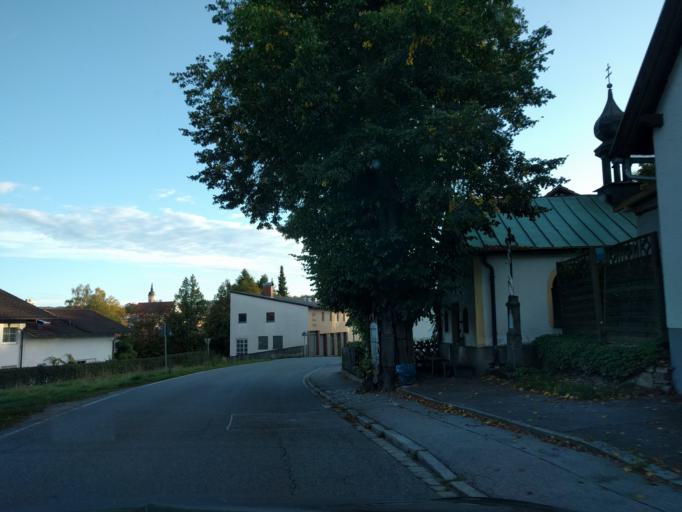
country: DE
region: Bavaria
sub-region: Lower Bavaria
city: Viechtach
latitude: 49.0848
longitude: 12.8849
